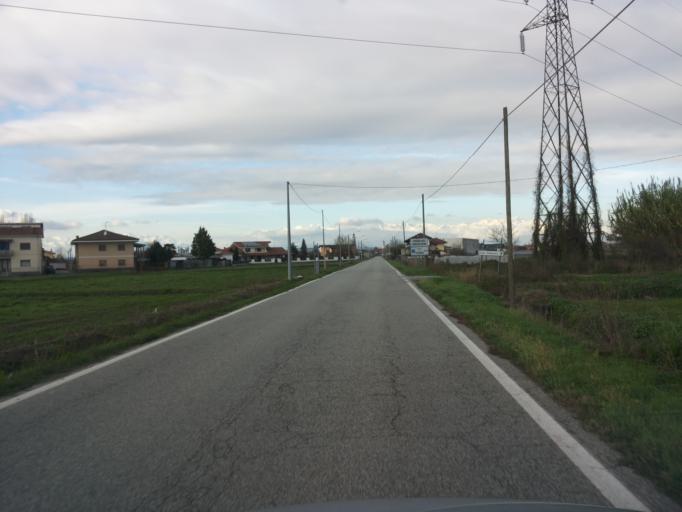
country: IT
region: Piedmont
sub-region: Provincia di Vercelli
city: Tronzano Vercellese
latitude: 45.3340
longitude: 8.1839
